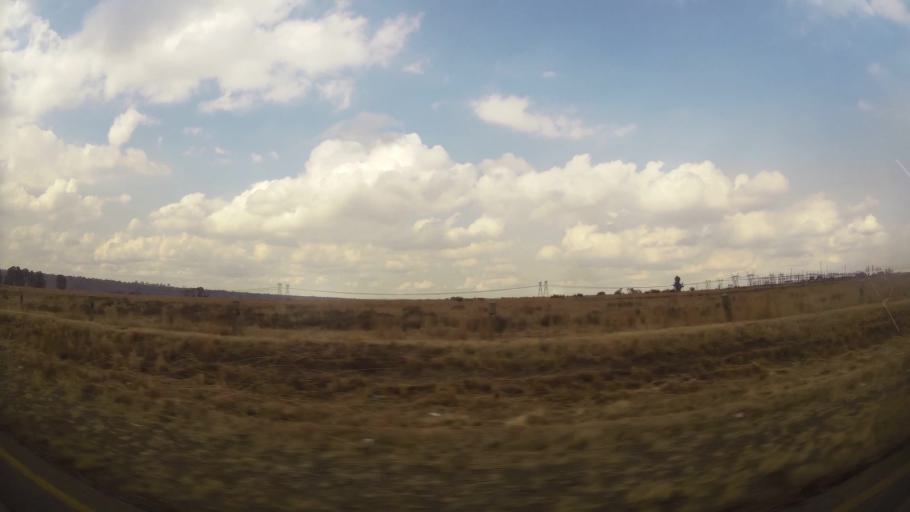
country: ZA
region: Orange Free State
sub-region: Fezile Dabi District Municipality
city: Sasolburg
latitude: -26.8156
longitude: 27.9074
